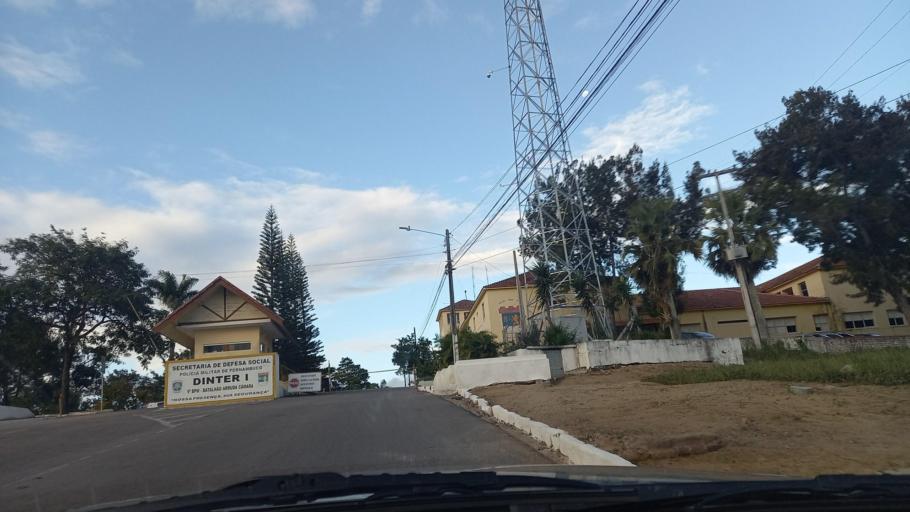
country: BR
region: Pernambuco
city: Garanhuns
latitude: -8.8796
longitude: -36.4722
